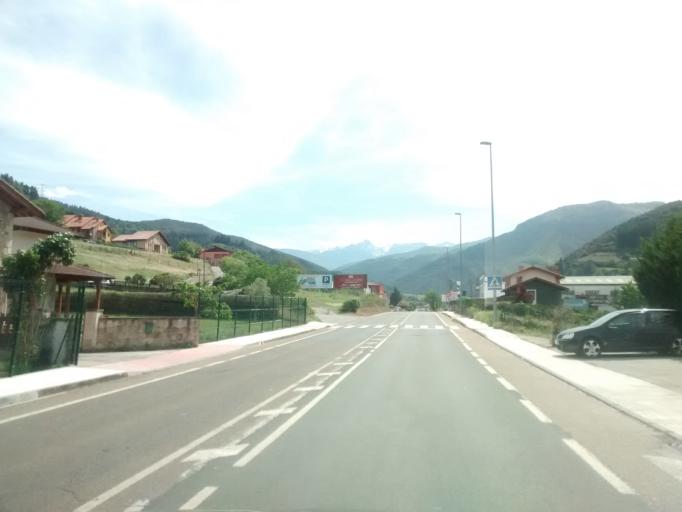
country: ES
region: Cantabria
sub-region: Provincia de Cantabria
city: Potes
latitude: 43.1667
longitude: -4.6064
